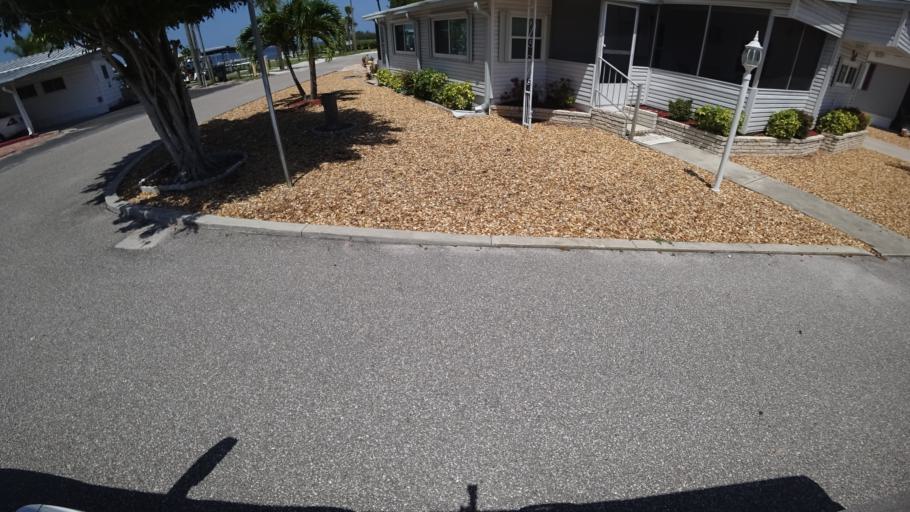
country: US
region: Florida
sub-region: Manatee County
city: Bayshore Gardens
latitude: 27.4169
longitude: -82.5815
